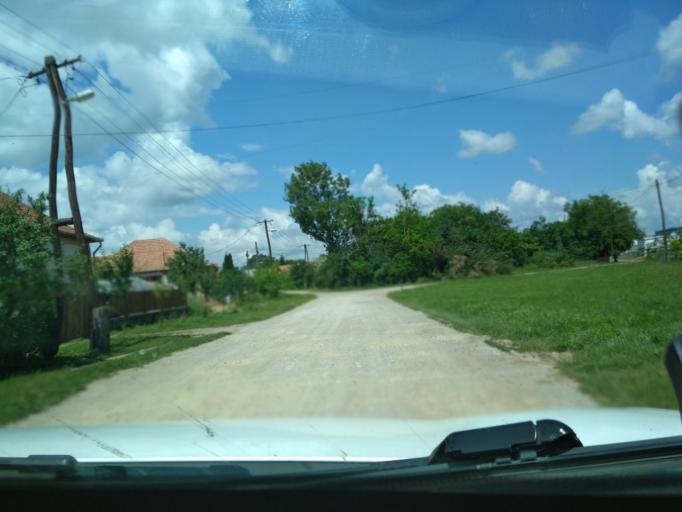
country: HU
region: Jasz-Nagykun-Szolnok
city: Tiszafured
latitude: 47.6040
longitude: 20.7589
